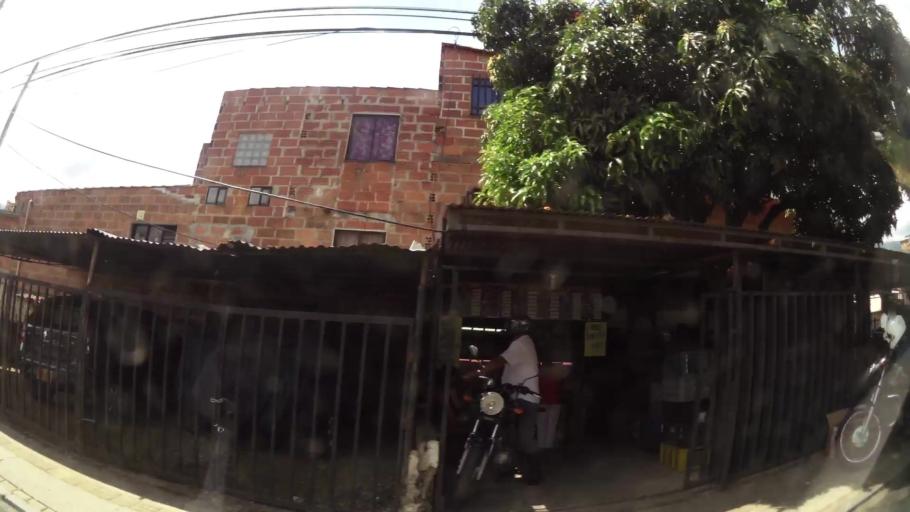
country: CO
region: Antioquia
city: Bello
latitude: 6.3443
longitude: -75.5542
